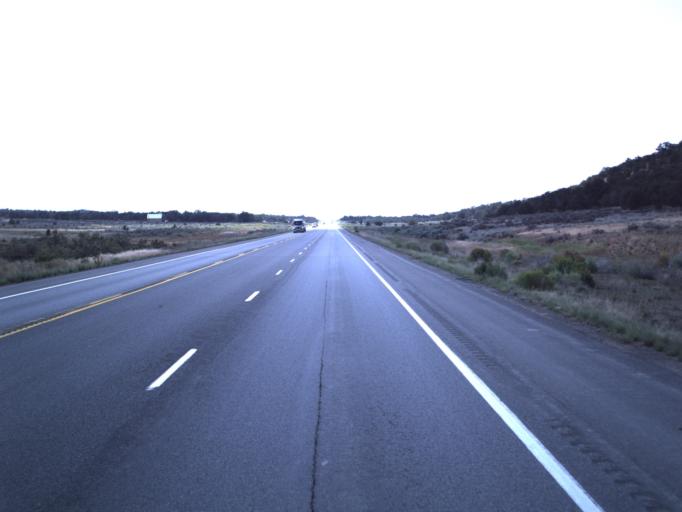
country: US
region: Utah
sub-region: Duchesne County
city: Duchesne
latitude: 40.1802
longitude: -110.6148
